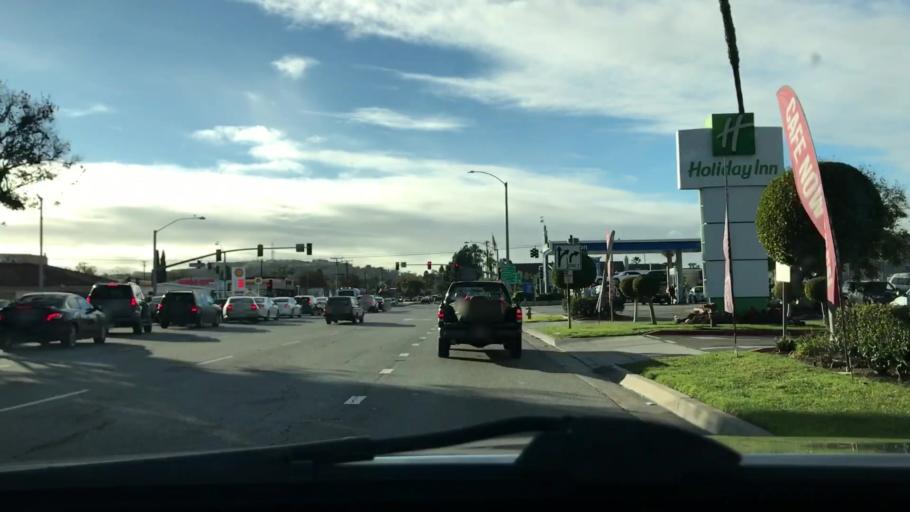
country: US
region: California
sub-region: Los Angeles County
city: Signal Hill
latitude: 33.8035
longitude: -118.1414
